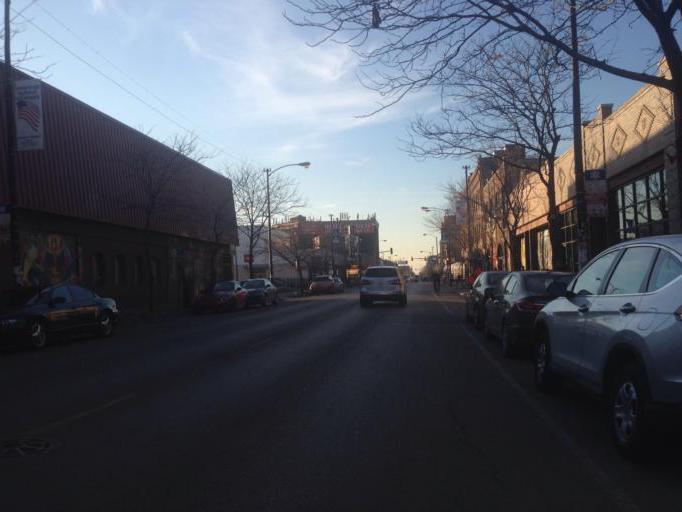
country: US
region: Illinois
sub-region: Cook County
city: Lincolnwood
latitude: 41.9240
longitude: -87.6991
